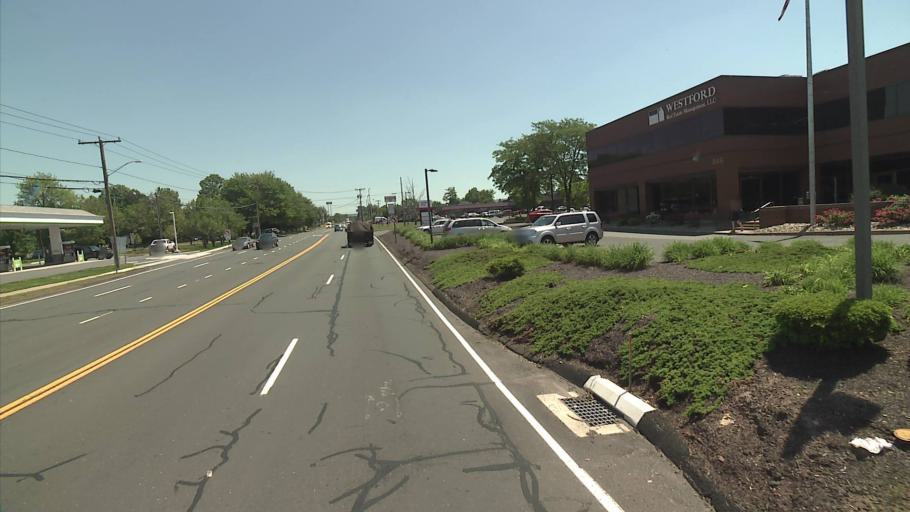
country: US
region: Connecticut
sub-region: Tolland County
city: Rockville
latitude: 41.8272
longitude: -72.4888
